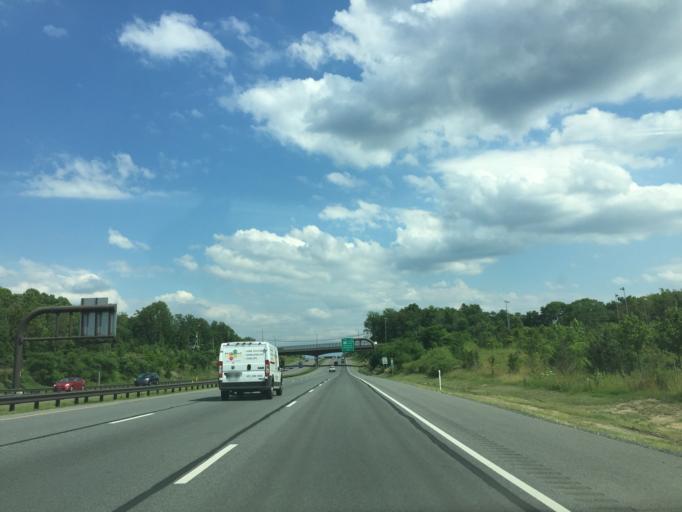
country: US
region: Maryland
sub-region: Montgomery County
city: Rossmoor
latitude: 39.1147
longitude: -77.0631
